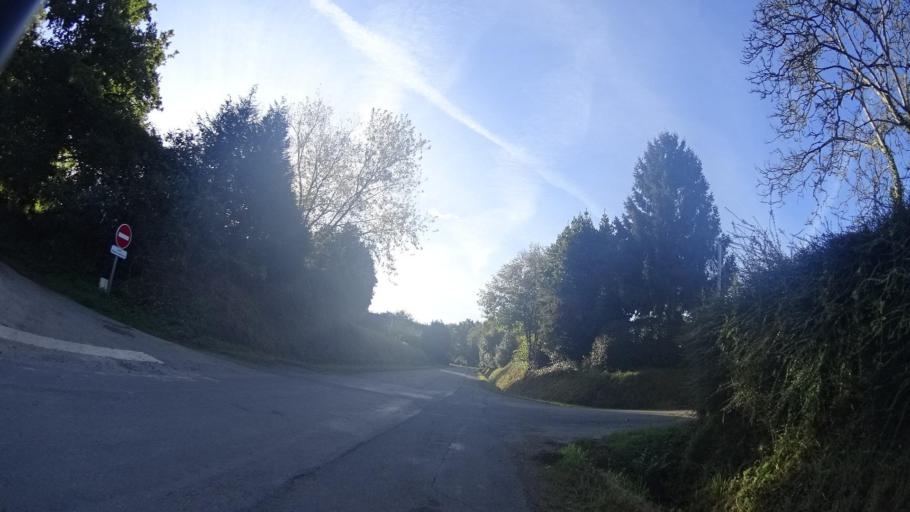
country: FR
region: Brittany
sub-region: Departement des Cotes-d'Armor
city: Evran
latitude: 48.3389
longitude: -1.9375
